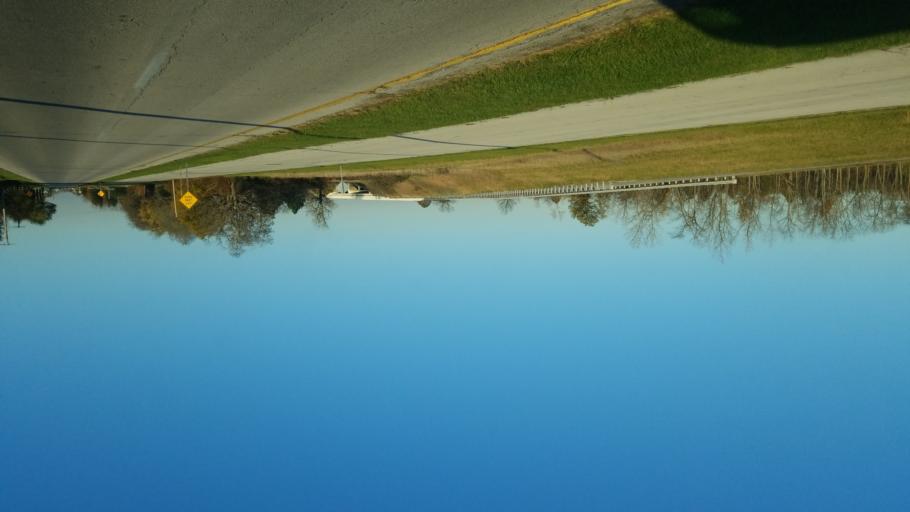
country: US
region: Ohio
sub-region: Sandusky County
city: Fremont
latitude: 41.3345
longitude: -83.0657
